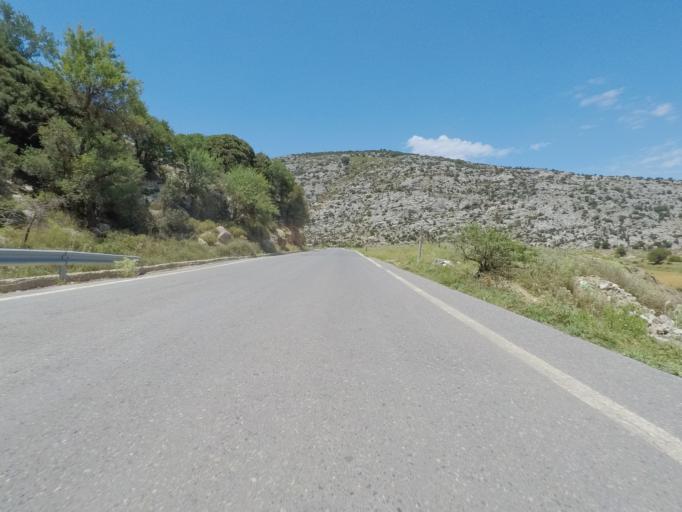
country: GR
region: Crete
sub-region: Nomos Irakleiou
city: Mokhos
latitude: 35.1910
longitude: 25.4322
